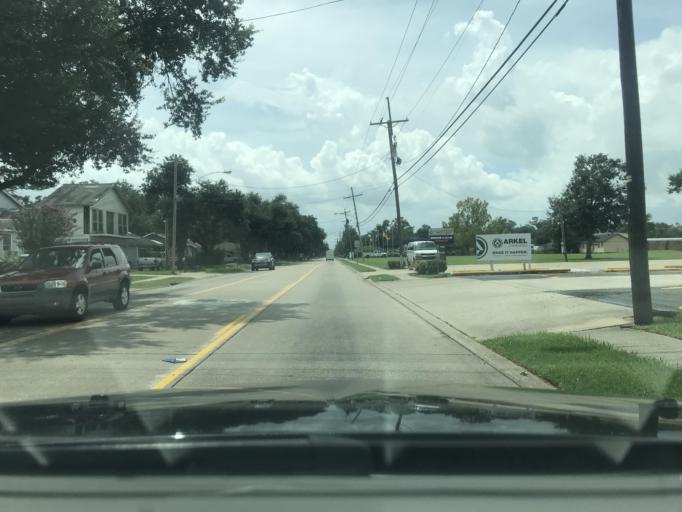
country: US
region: Louisiana
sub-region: Calcasieu Parish
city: Lake Charles
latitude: 30.2131
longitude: -93.1863
